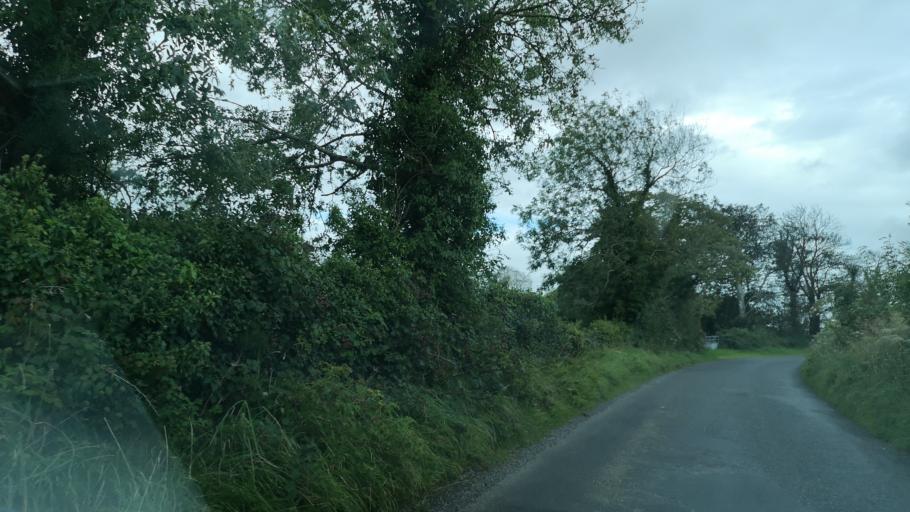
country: IE
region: Connaught
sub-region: County Galway
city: Loughrea
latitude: 53.3009
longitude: -8.6001
